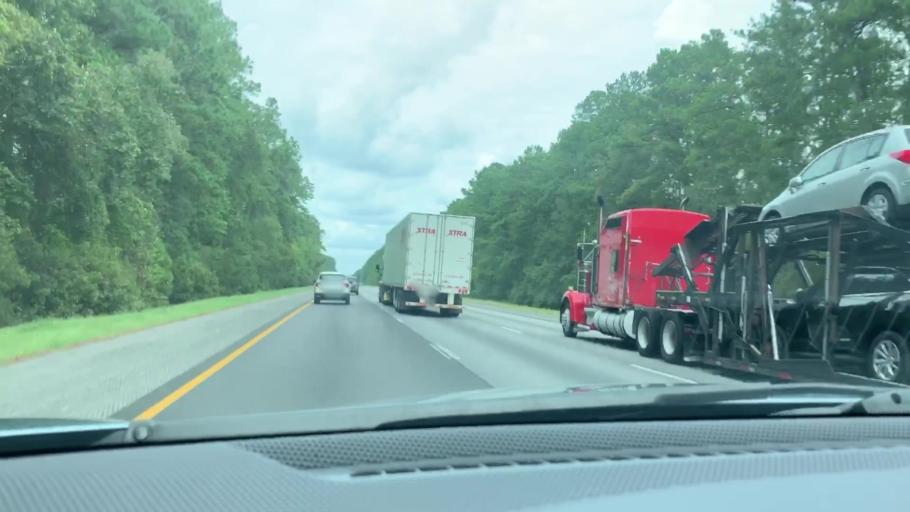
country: US
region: Georgia
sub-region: Bryan County
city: Richmond Hill
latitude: 31.8734
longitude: -81.3319
